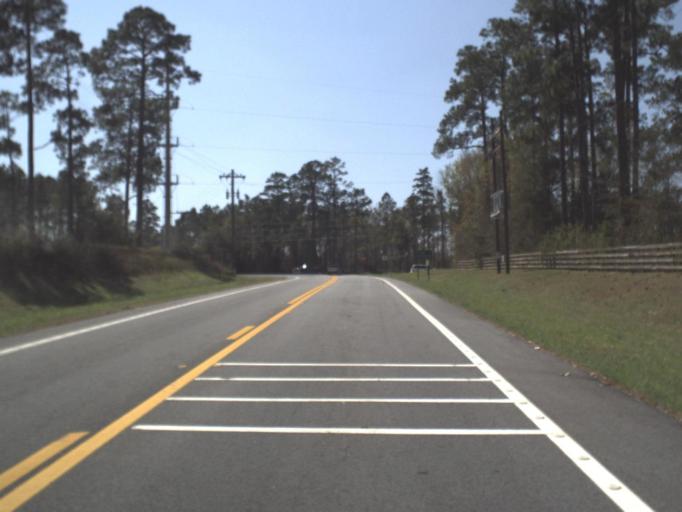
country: US
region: Florida
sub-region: Jefferson County
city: Monticello
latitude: 30.4062
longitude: -84.0210
